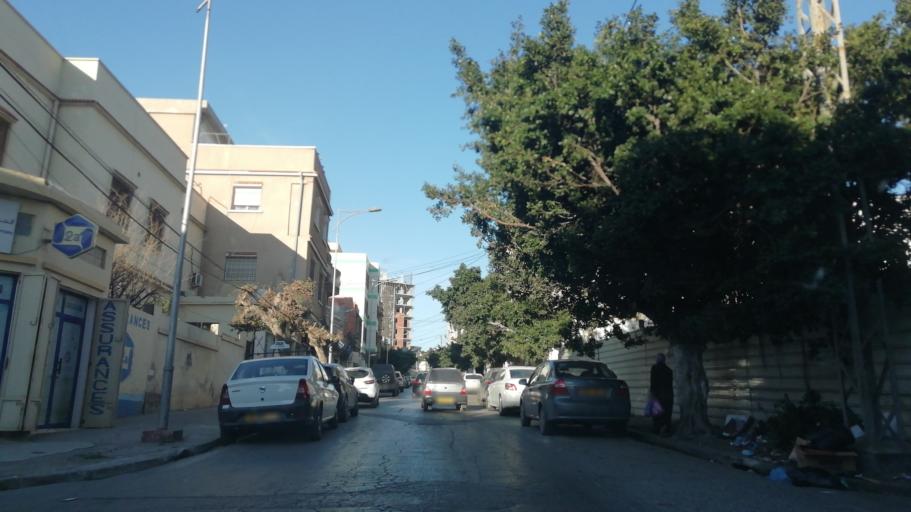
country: DZ
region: Oran
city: Oran
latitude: 35.7120
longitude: -0.6167
